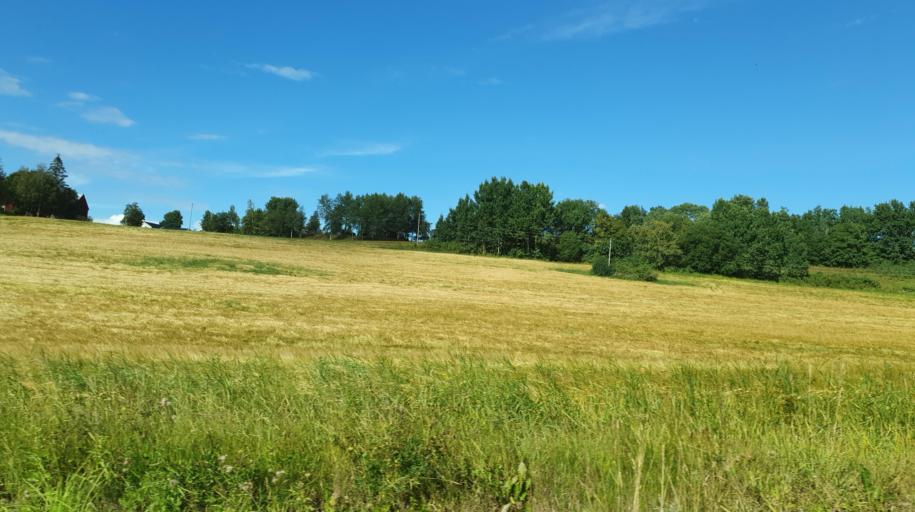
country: NO
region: Nord-Trondelag
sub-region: Levanger
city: Skogn
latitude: 63.7001
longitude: 11.2411
